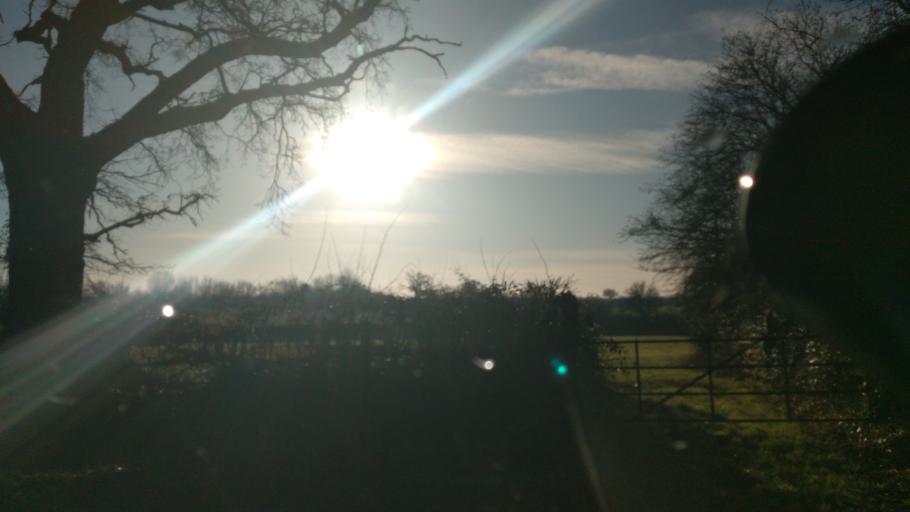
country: GB
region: England
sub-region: Wiltshire
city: Lacock
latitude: 51.4144
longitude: -2.1501
